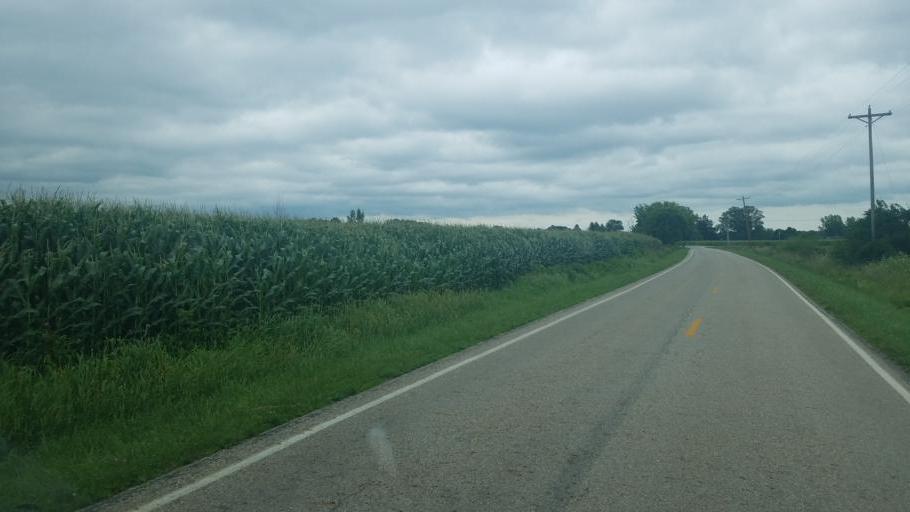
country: US
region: Ohio
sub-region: Pickaway County
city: Circleville
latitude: 39.6367
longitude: -82.9785
